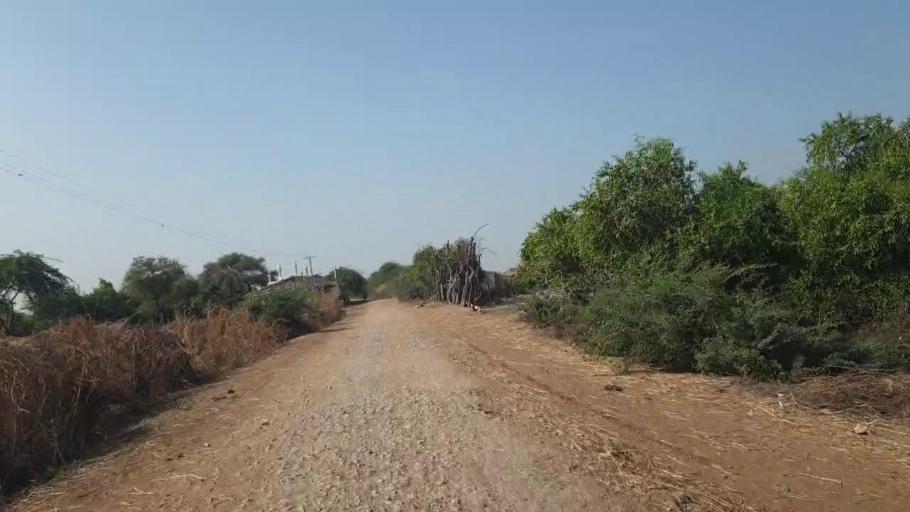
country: PK
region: Sindh
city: Badin
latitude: 24.5198
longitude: 68.7854
